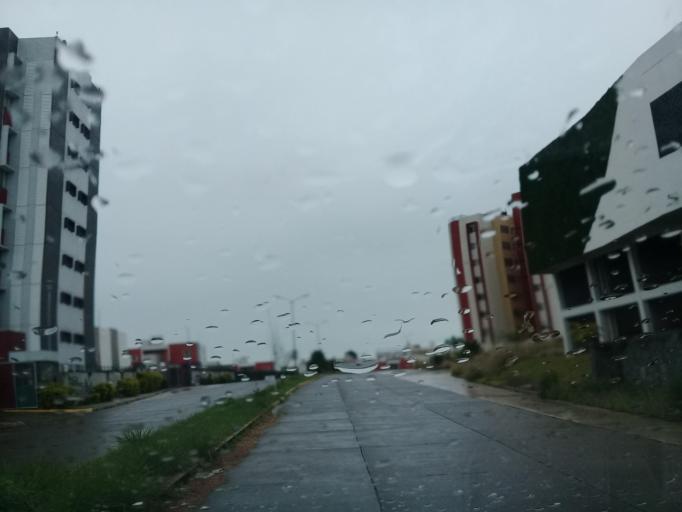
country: MX
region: Veracruz
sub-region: Emiliano Zapata
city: Las Trancas
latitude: 19.5043
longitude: -96.8563
